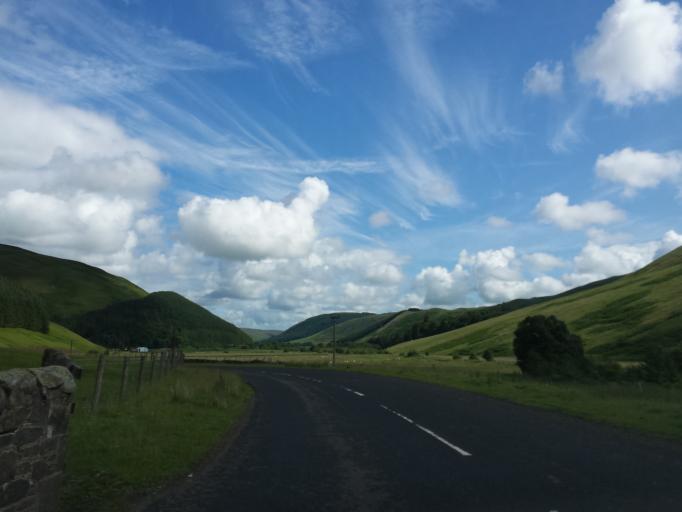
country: GB
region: Scotland
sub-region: The Scottish Borders
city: Peebles
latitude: 55.4503
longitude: -3.2216
